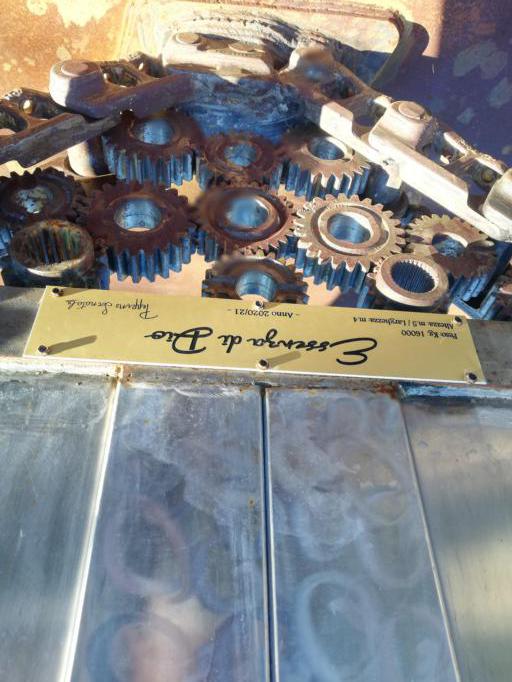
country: IT
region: Apulia
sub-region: Provincia di Bari
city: Poggiorsini
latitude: 40.8531
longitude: 16.3303
